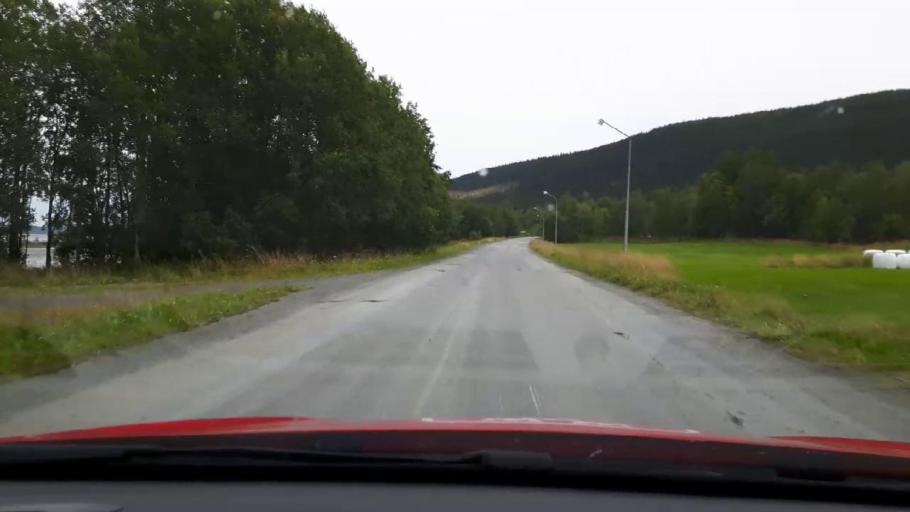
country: SE
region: Jaemtland
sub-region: Are Kommun
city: Are
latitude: 63.4937
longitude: 13.1241
